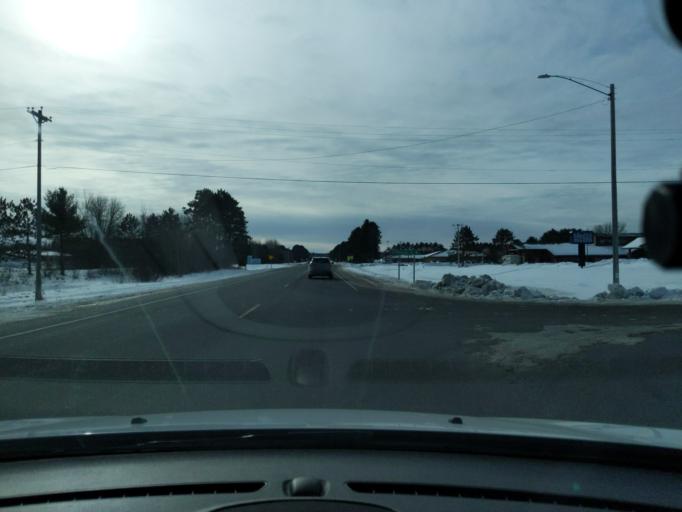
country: US
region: Wisconsin
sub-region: Washburn County
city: Shell Lake
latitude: 45.7338
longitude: -91.9292
